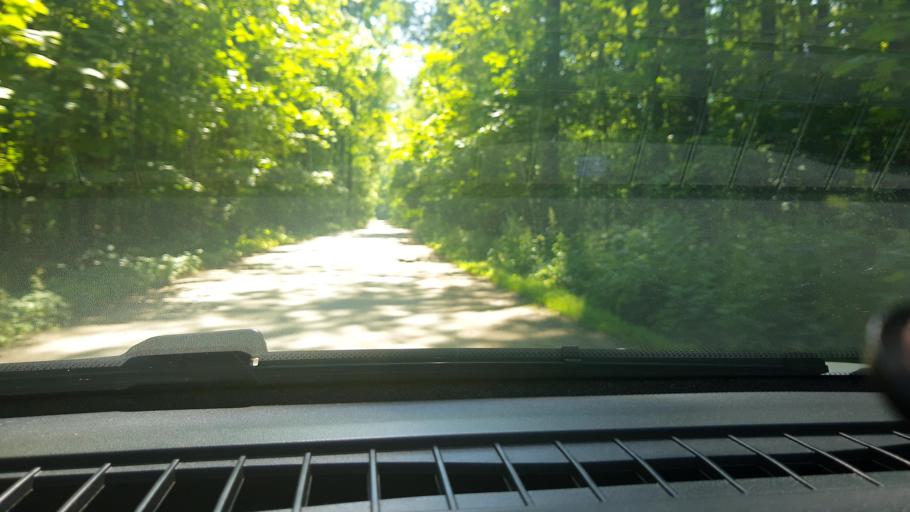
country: RU
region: Nizjnij Novgorod
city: Afonino
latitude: 56.2677
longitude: 44.1998
